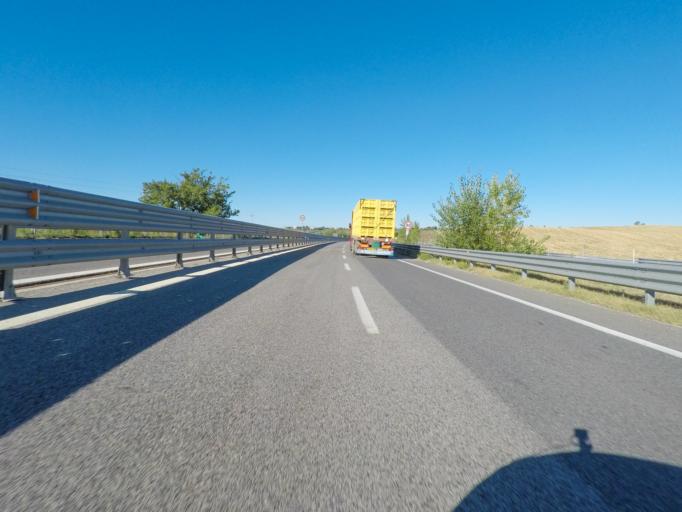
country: IT
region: Tuscany
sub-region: Provincia di Siena
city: Rosia
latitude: 43.2337
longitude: 11.2772
